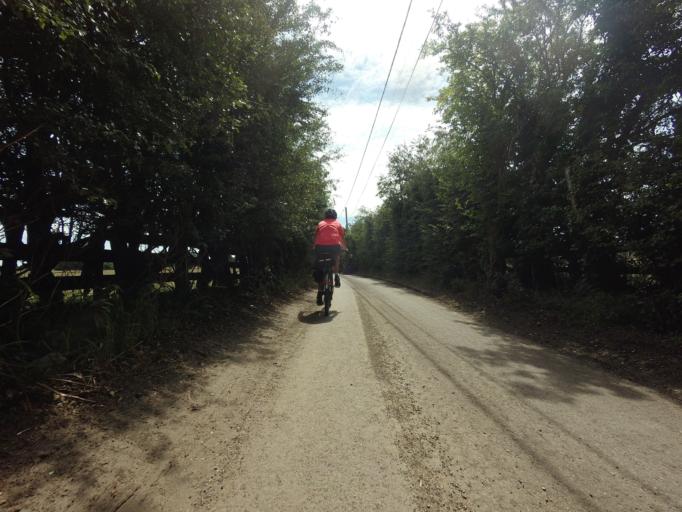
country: GB
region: England
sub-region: Kent
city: Stone
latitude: 51.0007
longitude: 0.8295
